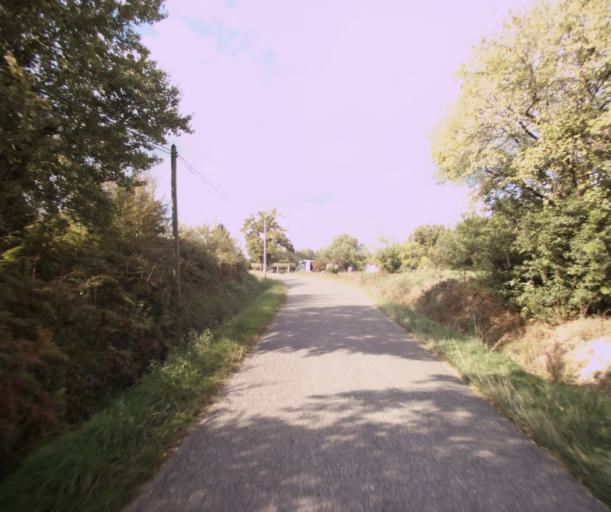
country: FR
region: Midi-Pyrenees
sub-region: Departement du Gers
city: Cazaubon
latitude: 43.8906
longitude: -0.0412
